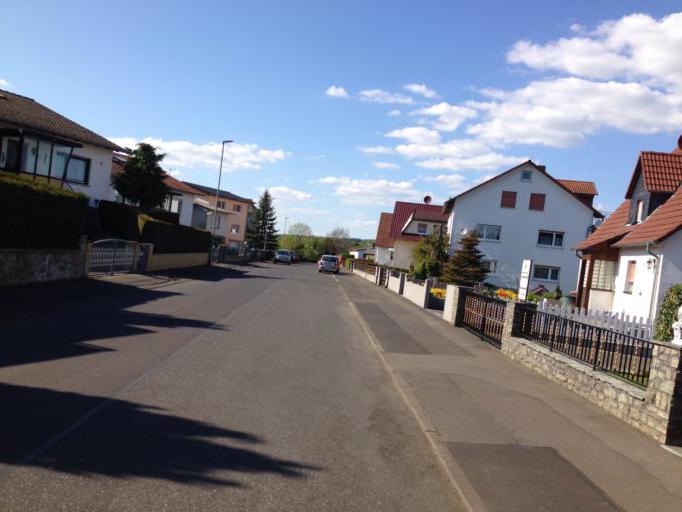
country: DE
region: Hesse
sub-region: Regierungsbezirk Giessen
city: Grunberg
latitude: 50.5603
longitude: 8.8984
